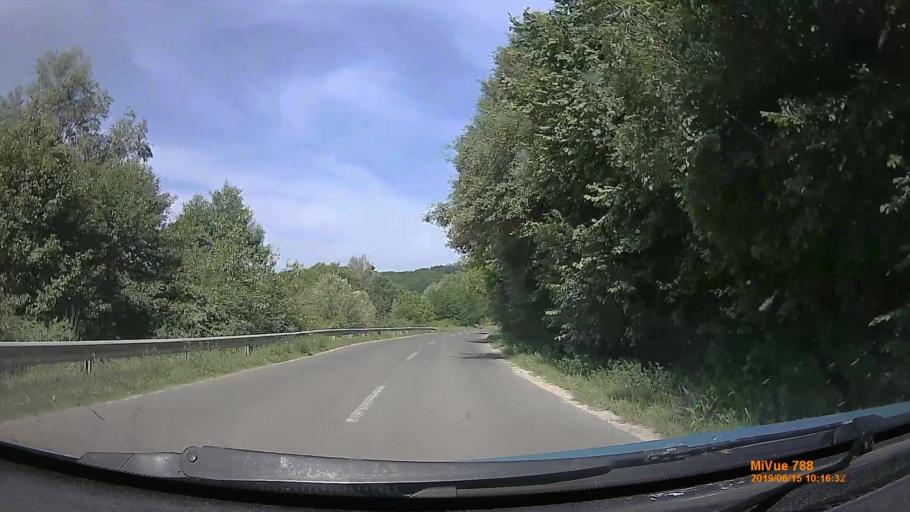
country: HU
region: Baranya
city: Buekkoesd
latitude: 46.1280
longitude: 18.0205
